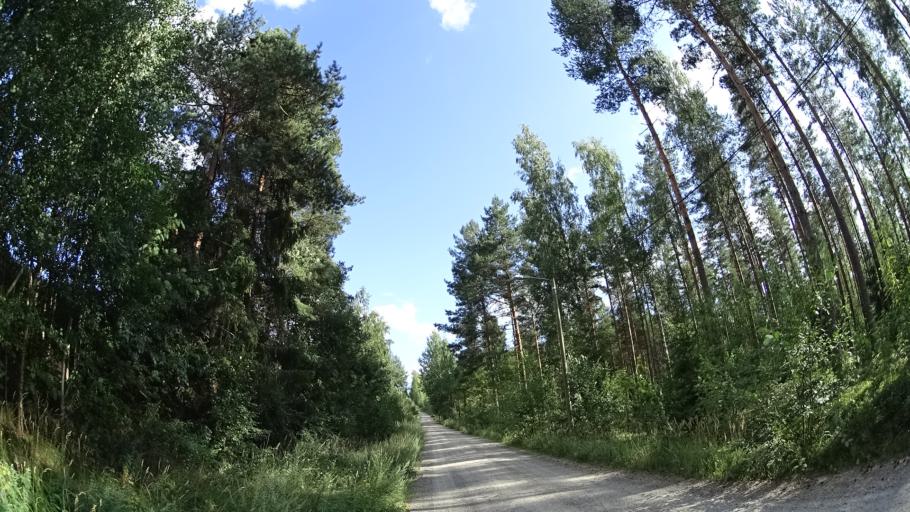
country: FI
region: Uusimaa
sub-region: Helsinki
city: Vihti
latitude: 60.3657
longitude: 24.3508
